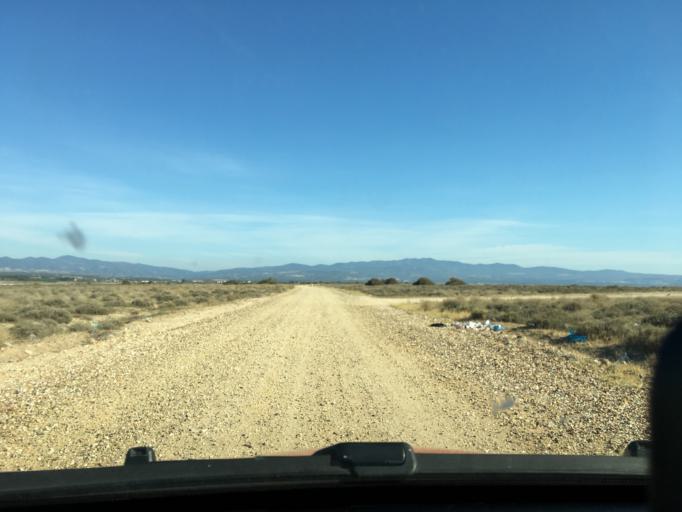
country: GR
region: Central Macedonia
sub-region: Nomos Chalkidikis
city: Nea Potidhaia
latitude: 40.2218
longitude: 23.3350
